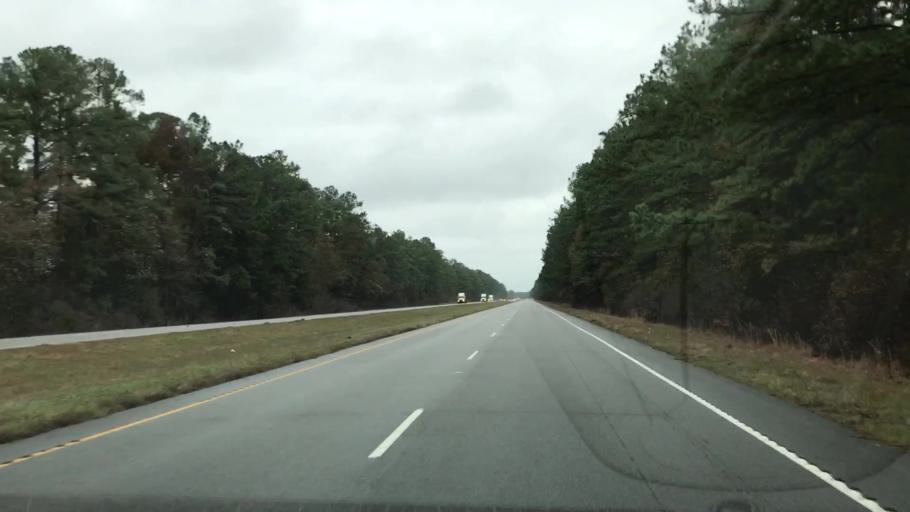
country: US
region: South Carolina
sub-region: Charleston County
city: Awendaw
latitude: 33.1595
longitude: -79.4268
